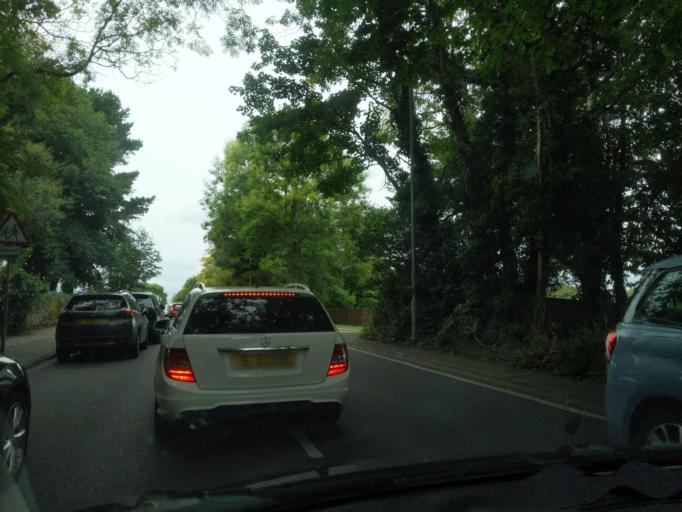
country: GB
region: England
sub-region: Cornwall
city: St Austell
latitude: 50.3375
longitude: -4.7666
